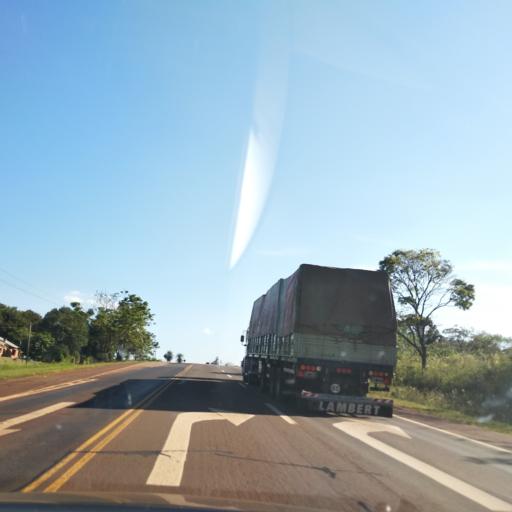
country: AR
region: Misiones
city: Jardin America
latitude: -27.0971
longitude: -55.3023
